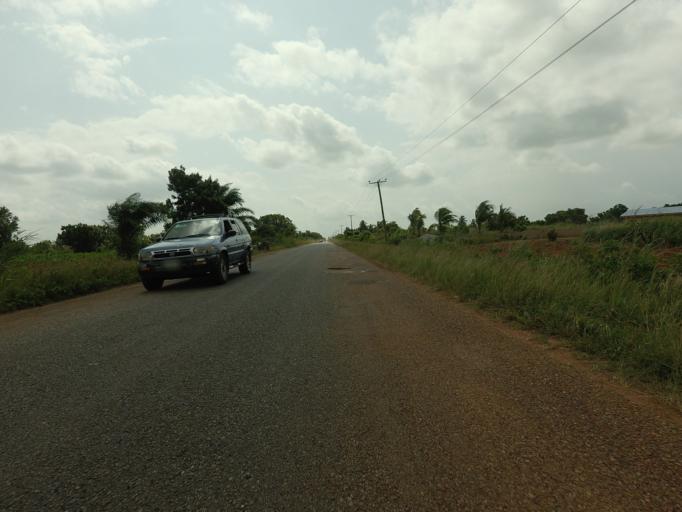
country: TG
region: Maritime
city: Lome
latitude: 6.1845
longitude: 1.0655
